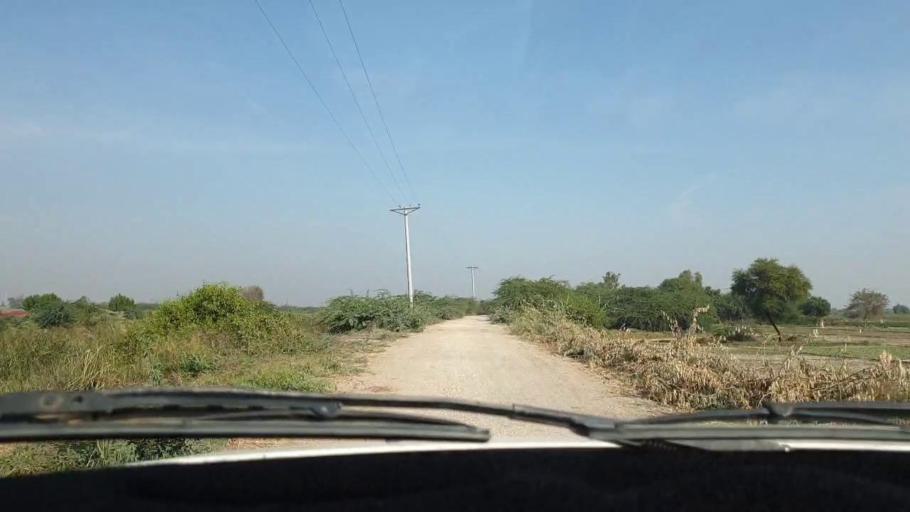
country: PK
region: Sindh
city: Bulri
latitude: 24.9710
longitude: 68.4564
